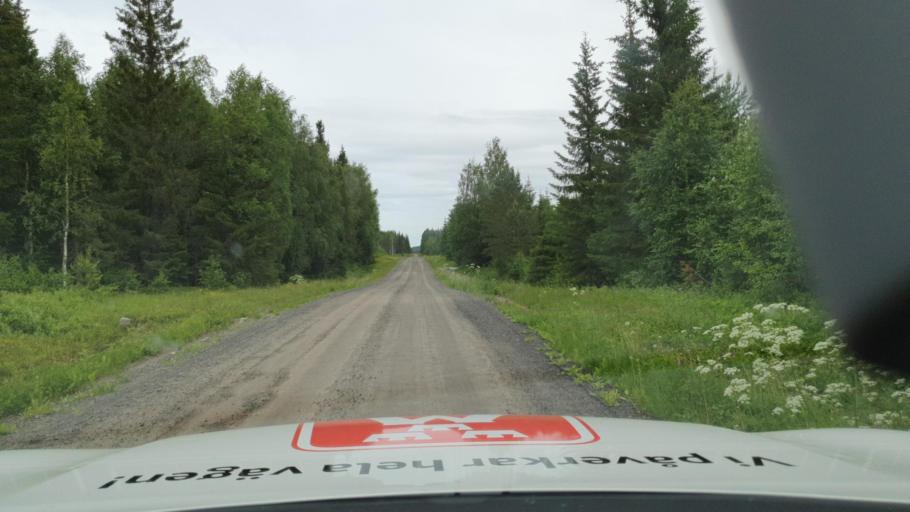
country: SE
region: Vaesterbotten
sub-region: Skelleftea Kommun
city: Burtraesk
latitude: 64.3711
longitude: 20.6161
